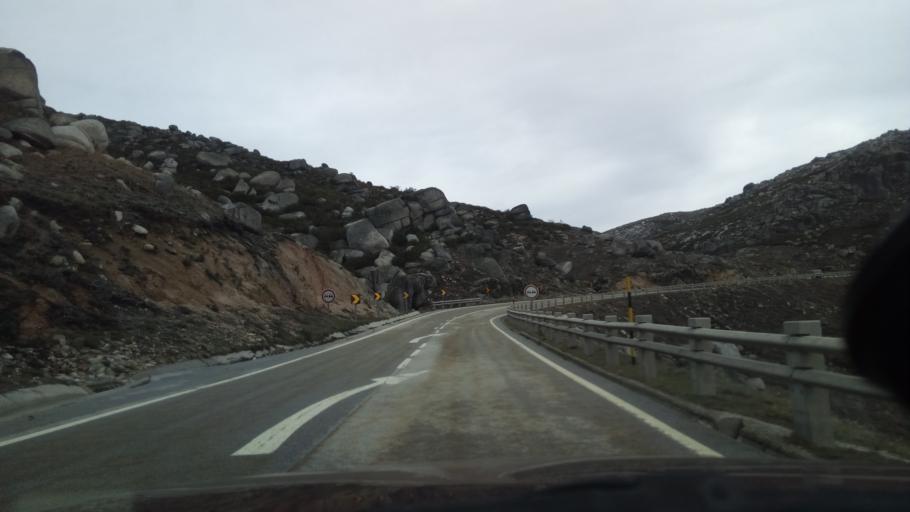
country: PT
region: Guarda
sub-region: Seia
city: Seia
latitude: 40.3558
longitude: -7.6796
